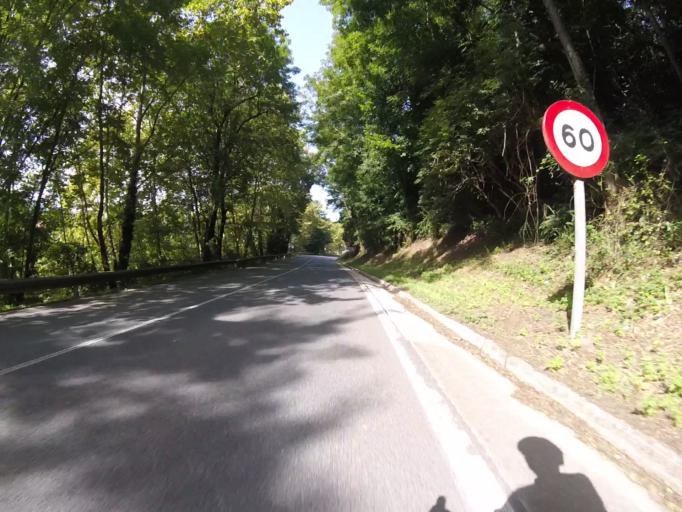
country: ES
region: Navarre
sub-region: Provincia de Navarra
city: Doneztebe
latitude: 43.1341
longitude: -1.6624
